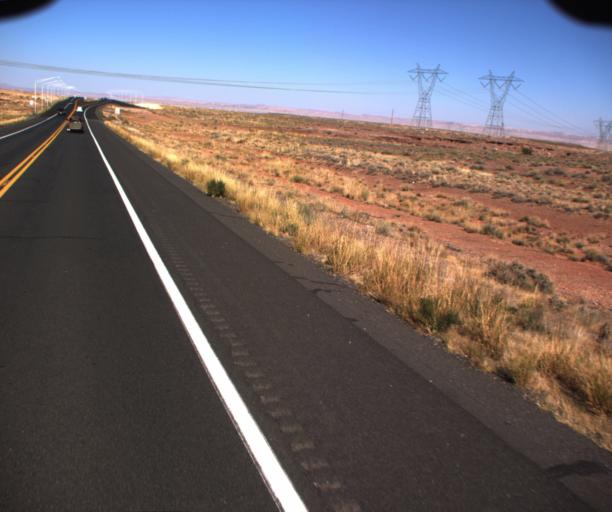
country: US
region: Arizona
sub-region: Coconino County
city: Tuba City
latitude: 35.8320
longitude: -111.4379
